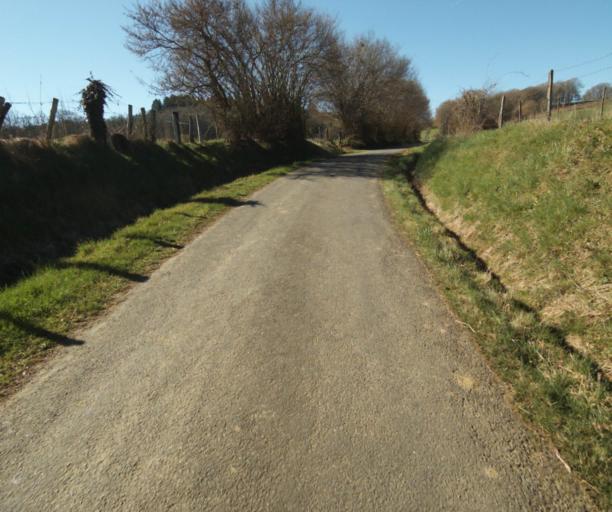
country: FR
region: Limousin
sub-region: Departement de la Correze
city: Chamboulive
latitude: 45.4174
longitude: 1.7049
